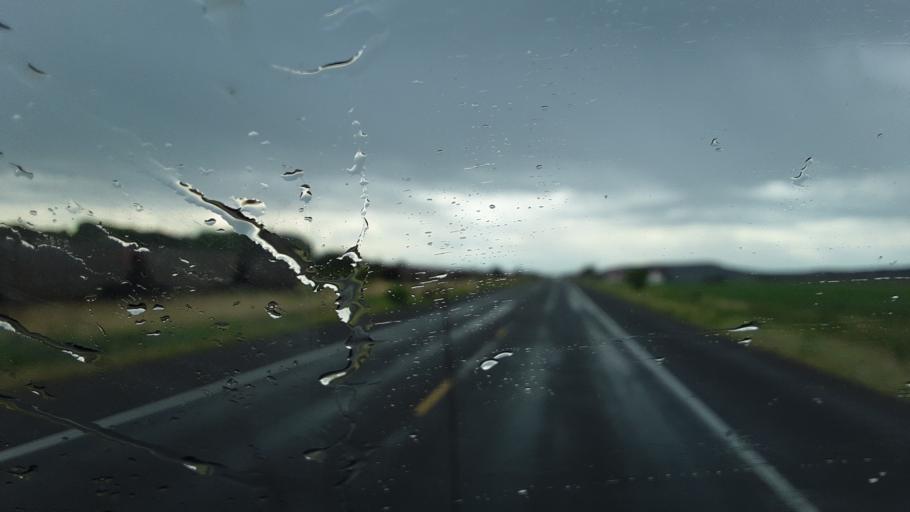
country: US
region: Colorado
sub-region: Rio Grande County
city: Del Norte
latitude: 37.6746
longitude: -106.3280
